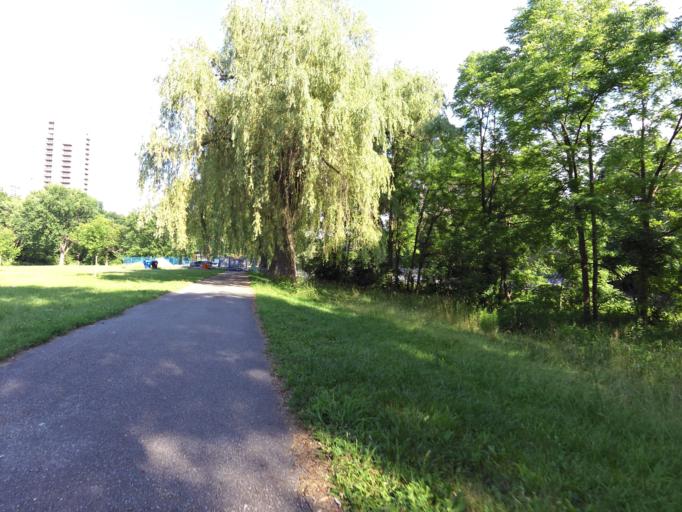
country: CA
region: Ontario
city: Etobicoke
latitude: 43.7020
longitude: -79.5261
